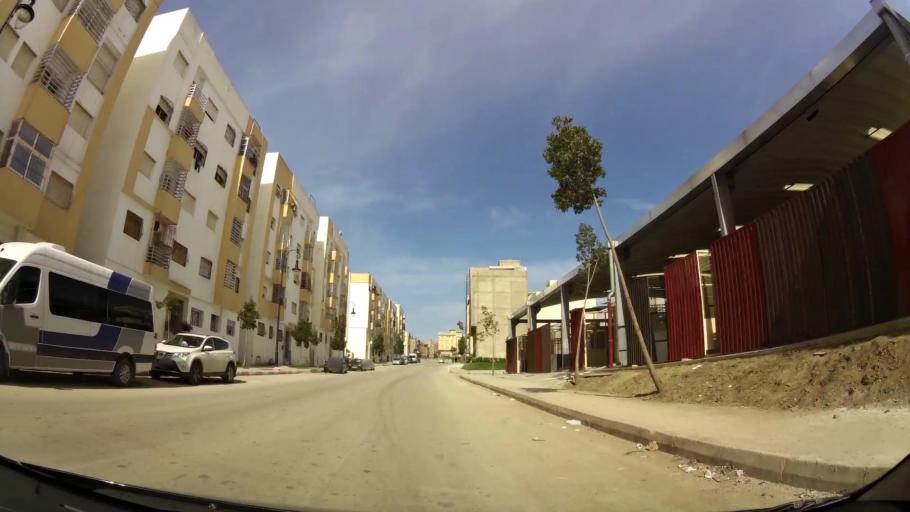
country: MA
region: Tanger-Tetouan
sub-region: Tanger-Assilah
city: Tangier
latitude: 35.7244
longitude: -5.8077
